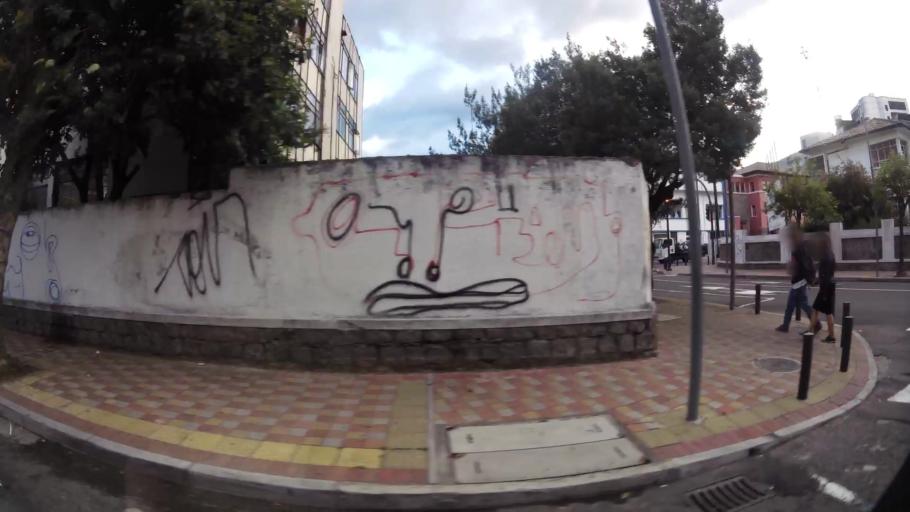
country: EC
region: Pichincha
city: Quito
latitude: -0.2043
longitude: -78.4924
